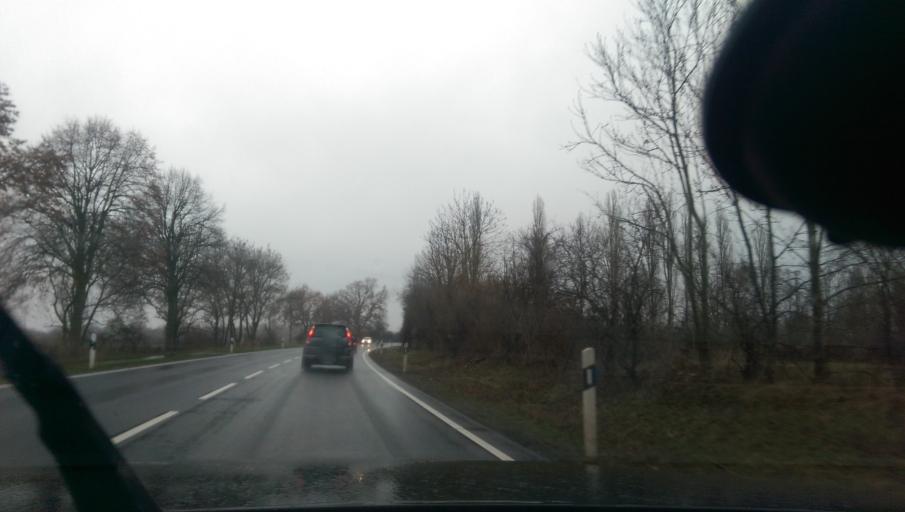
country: DE
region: Lower Saxony
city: Dorverden
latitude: 52.8795
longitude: 9.2187
